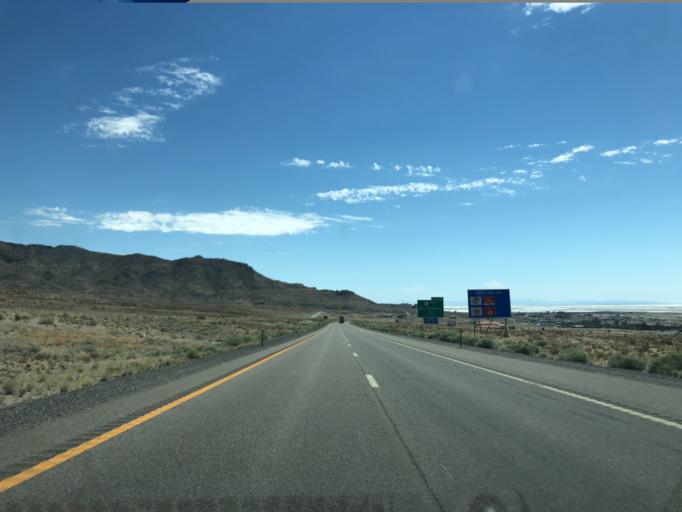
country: US
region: Nevada
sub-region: Elko County
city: West Wendover
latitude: 40.7443
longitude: -114.0825
